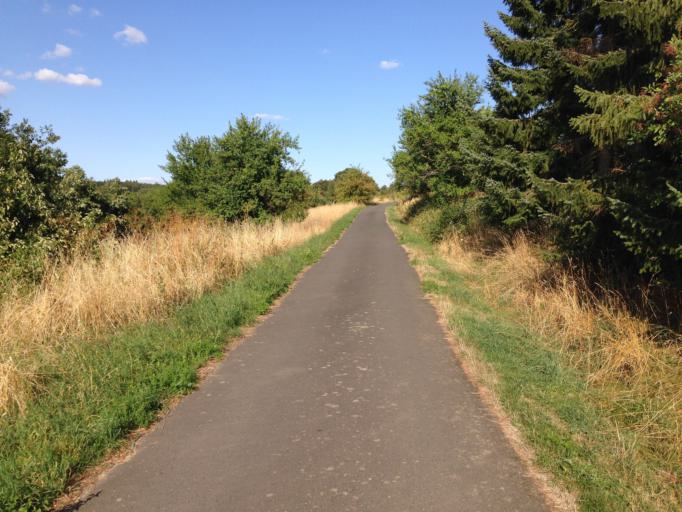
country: DE
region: Hesse
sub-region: Regierungsbezirk Giessen
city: Reiskirchen
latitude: 50.6187
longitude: 8.8565
